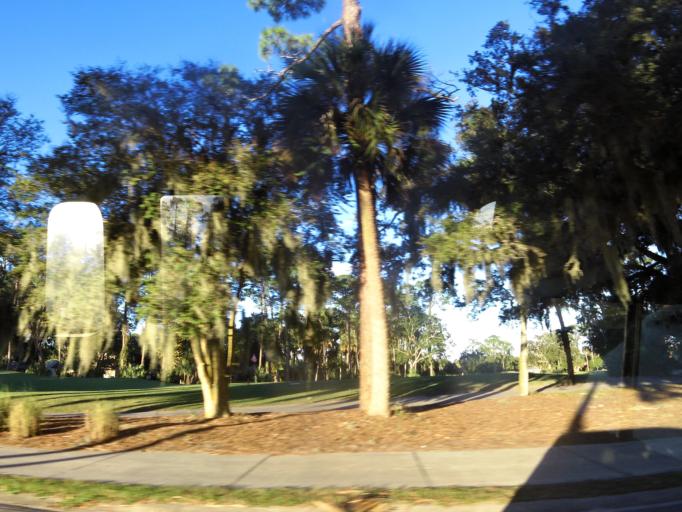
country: US
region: Florida
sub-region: Flagler County
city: Palm Coast
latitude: 29.5696
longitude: -81.1964
